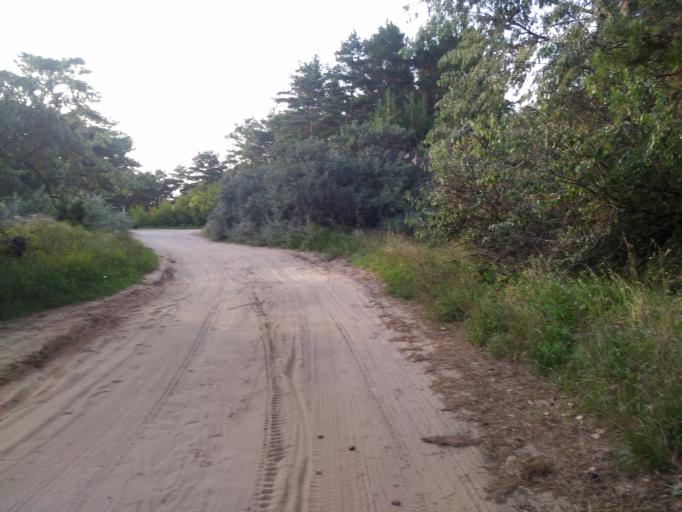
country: RU
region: Ulyanovsk
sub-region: Ulyanovskiy Rayon
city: Ulyanovsk
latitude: 54.3582
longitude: 48.5140
